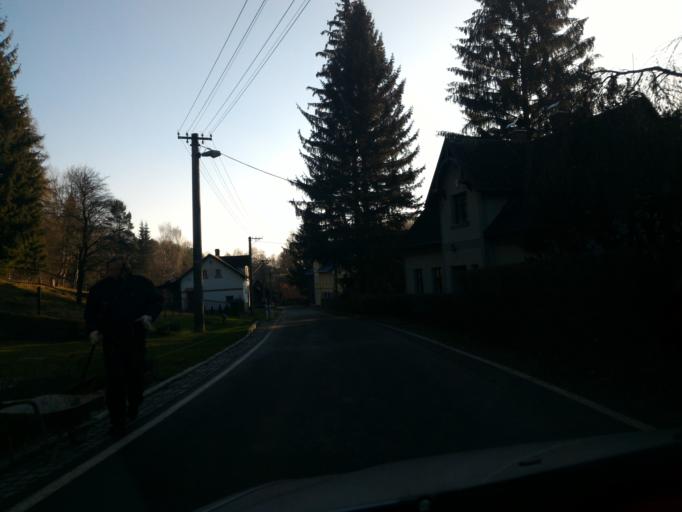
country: DE
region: Saxony
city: Kurort Oybin
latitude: 50.8041
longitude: 14.7175
